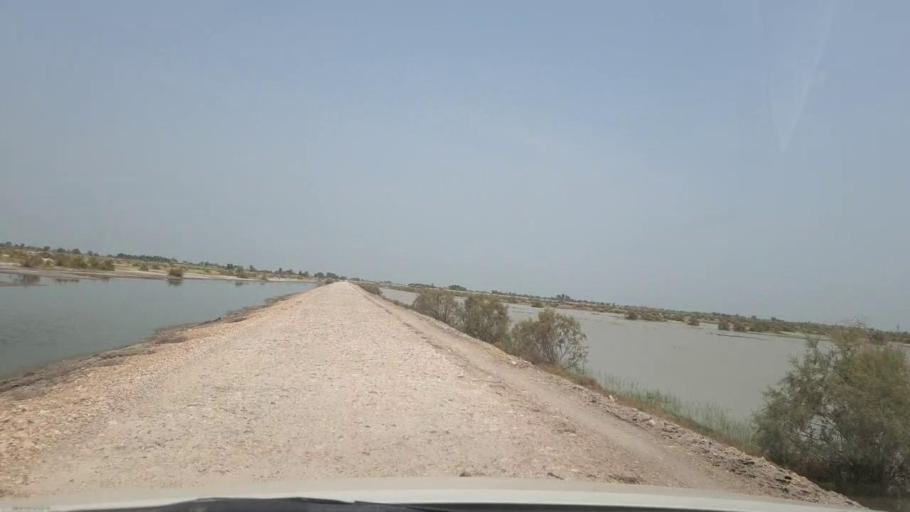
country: PK
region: Sindh
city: Rustam jo Goth
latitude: 28.0673
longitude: 68.8172
